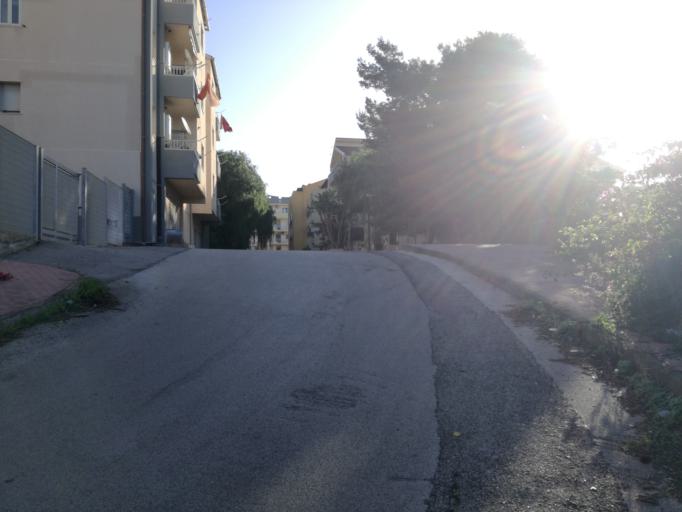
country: IT
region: Sicily
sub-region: Provincia di Caltanissetta
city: Gela
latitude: 37.0748
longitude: 14.2253
